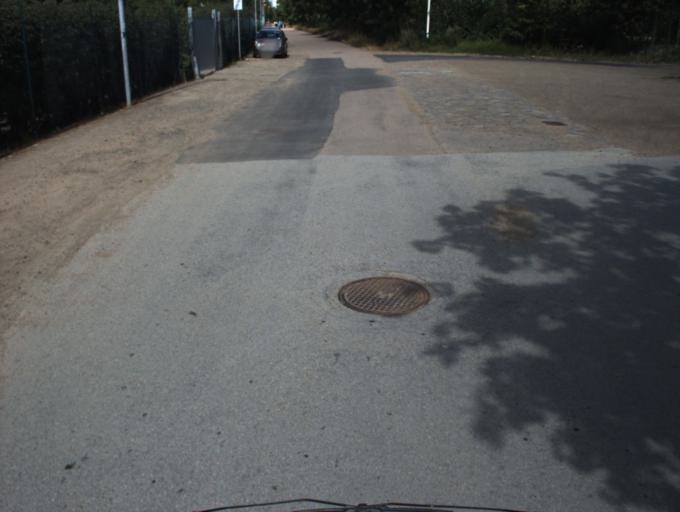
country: SE
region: Skane
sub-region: Helsingborg
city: Helsingborg
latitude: 56.0565
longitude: 12.7309
